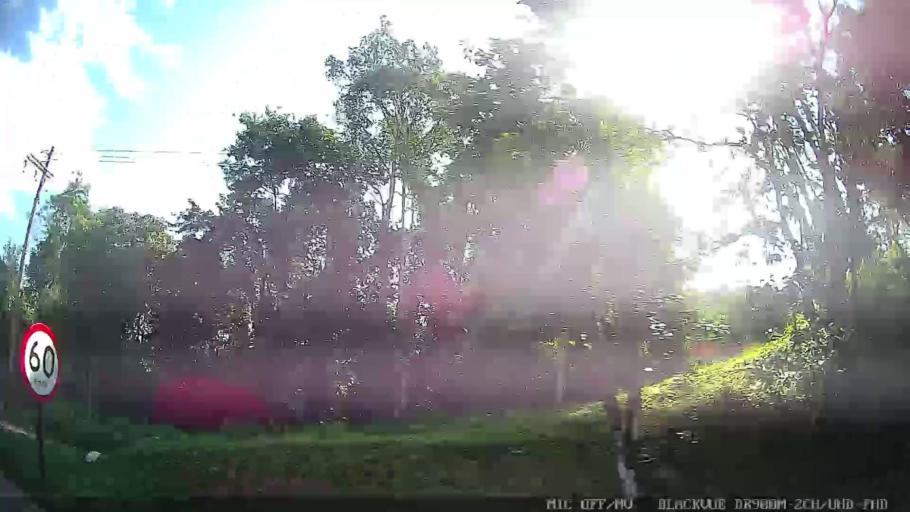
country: BR
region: Sao Paulo
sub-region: Santos
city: Santos
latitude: -23.9130
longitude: -46.2813
